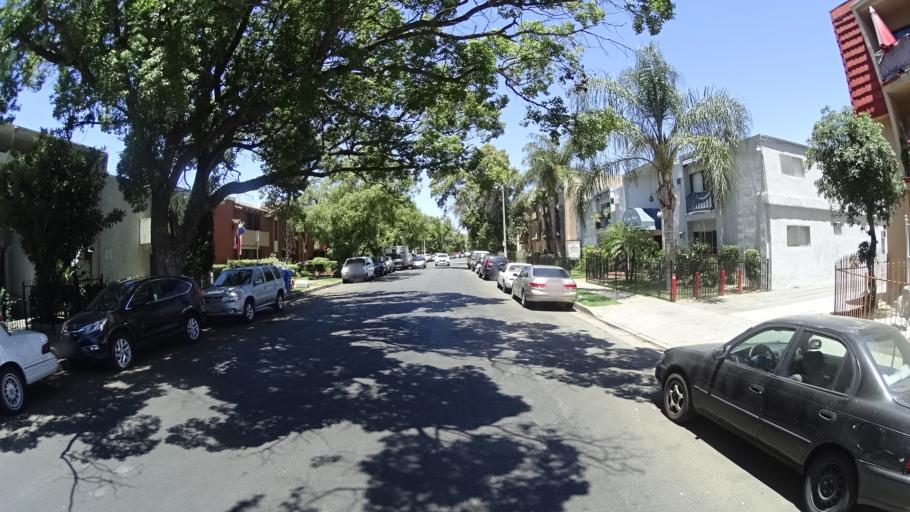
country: US
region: California
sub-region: Los Angeles County
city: Van Nuys
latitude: 34.2183
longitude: -118.4693
